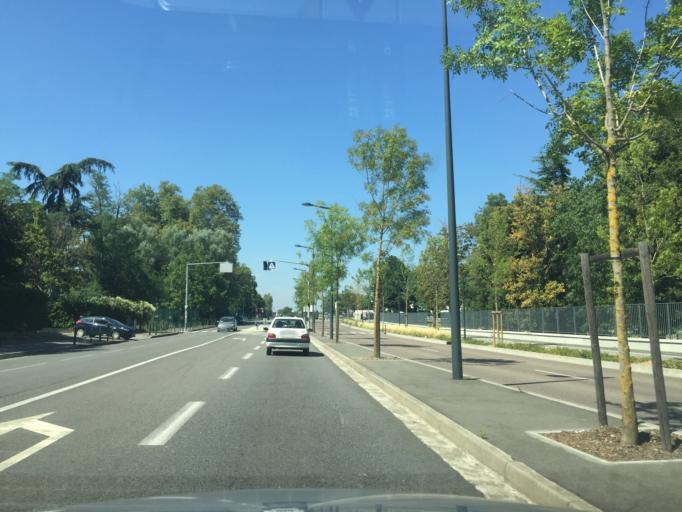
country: FR
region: Midi-Pyrenees
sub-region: Departement de la Haute-Garonne
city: Ramonville-Saint-Agne
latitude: 43.5584
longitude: 1.4642
